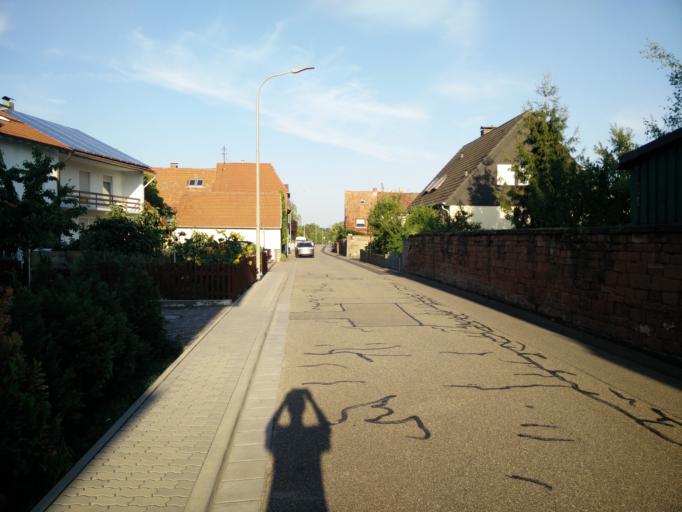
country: DE
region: Rheinland-Pfalz
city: Barbelroth
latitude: 49.1018
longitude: 8.0723
